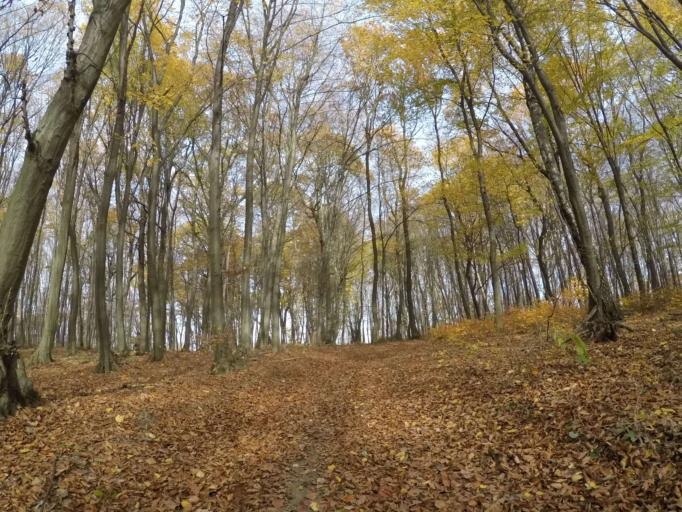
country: SK
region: Presovsky
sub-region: Okres Presov
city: Presov
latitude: 48.9352
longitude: 21.2198
